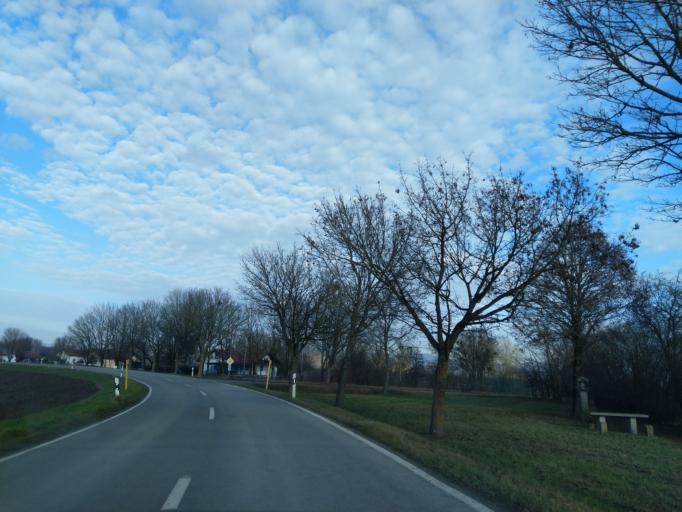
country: DE
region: Bavaria
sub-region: Lower Bavaria
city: Niederalteich
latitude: 48.7531
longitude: 13.0240
